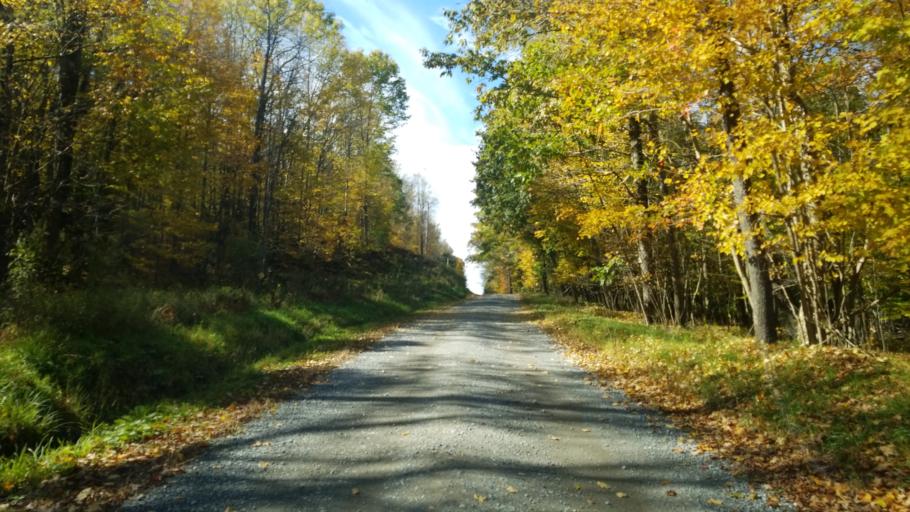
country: US
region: Pennsylvania
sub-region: Jefferson County
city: Falls Creek
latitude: 41.1918
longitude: -78.7878
